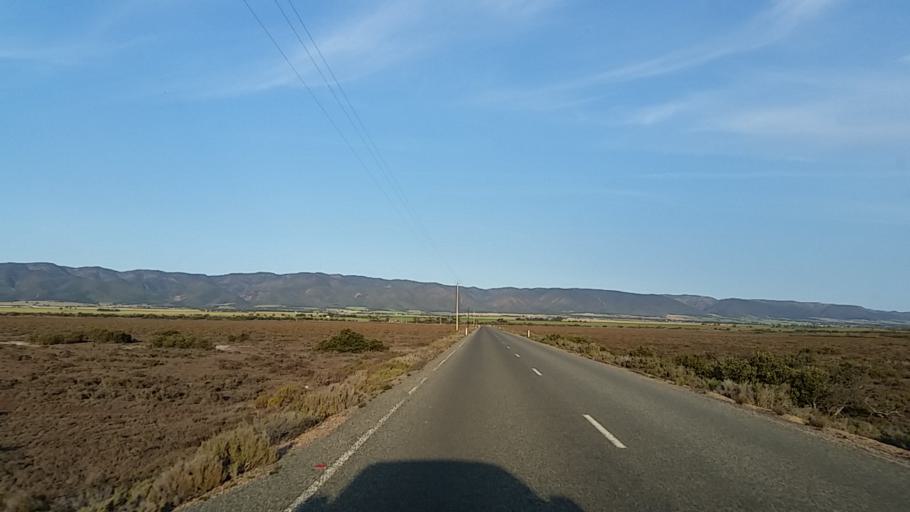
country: AU
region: South Australia
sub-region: Port Pirie City and Dists
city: Port Pirie
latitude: -33.1026
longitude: 138.0421
